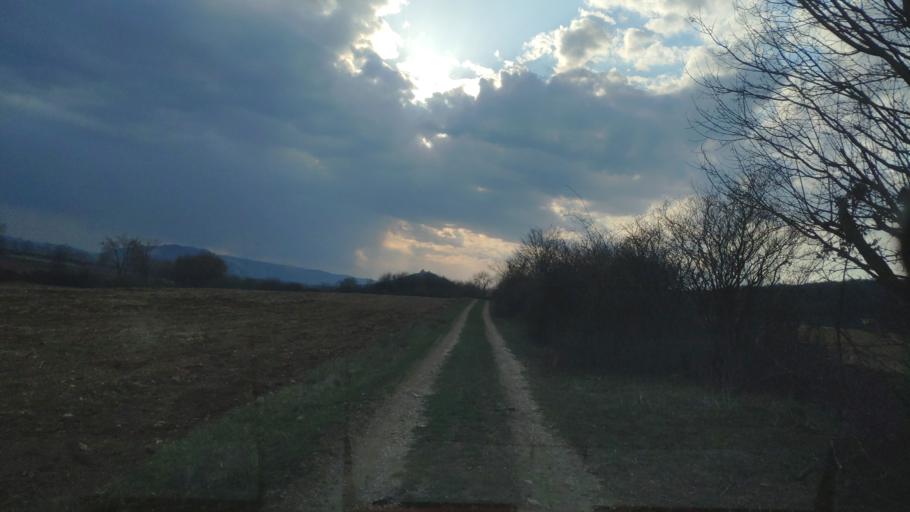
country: SK
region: Kosicky
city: Moldava nad Bodvou
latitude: 48.6176
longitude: 20.9260
